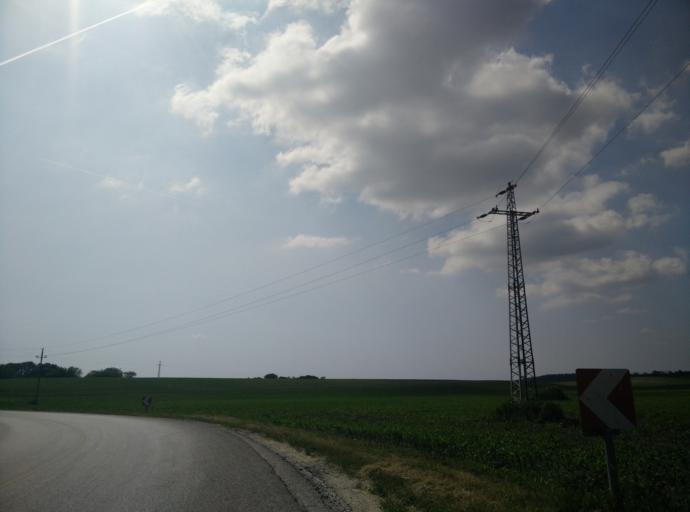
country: HU
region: Pest
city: Biatorbagy
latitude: 47.4748
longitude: 18.7994
